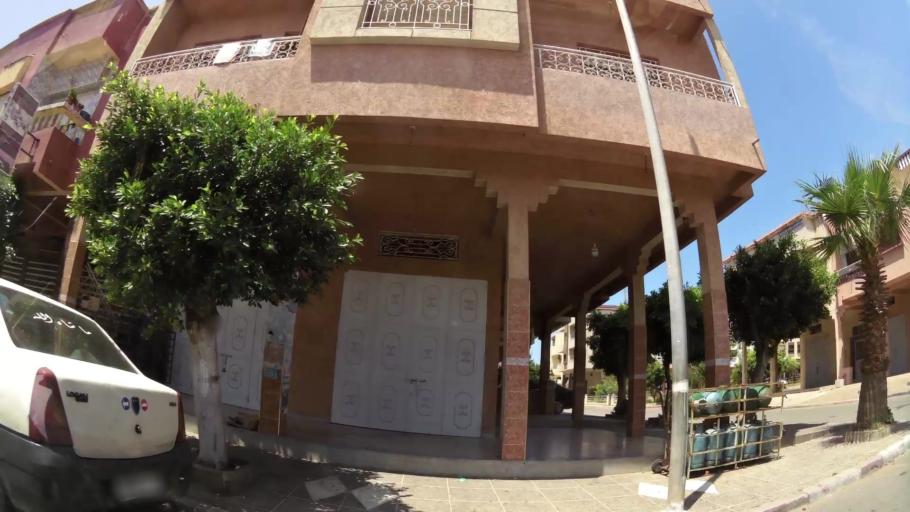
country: MA
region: Gharb-Chrarda-Beni Hssen
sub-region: Kenitra Province
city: Kenitra
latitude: 34.2689
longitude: -6.6137
